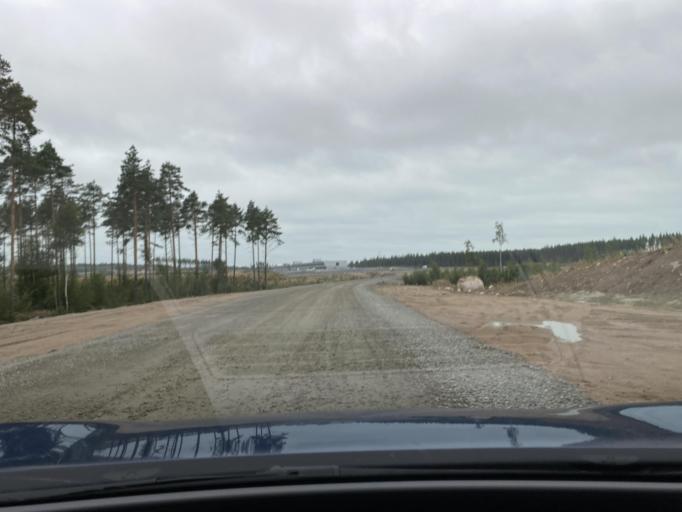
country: FI
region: Kymenlaakso
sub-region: Kouvola
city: Iitti
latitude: 60.8777
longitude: 26.4927
